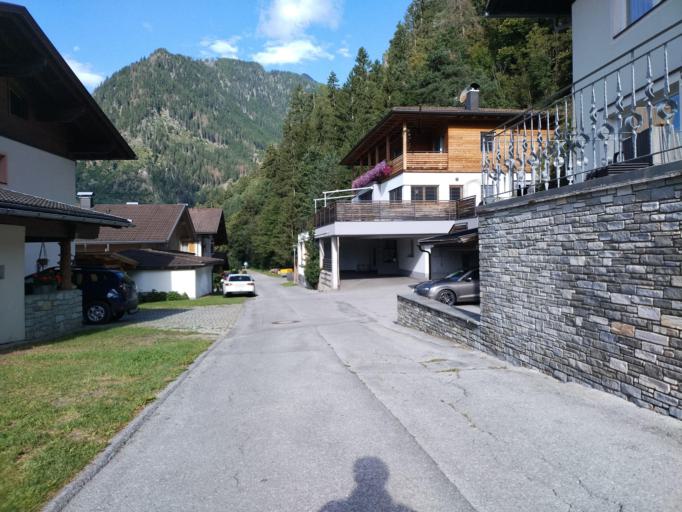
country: AT
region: Tyrol
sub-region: Politischer Bezirk Lienz
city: Hopfgarten in Defereggen
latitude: 46.9308
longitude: 12.5894
